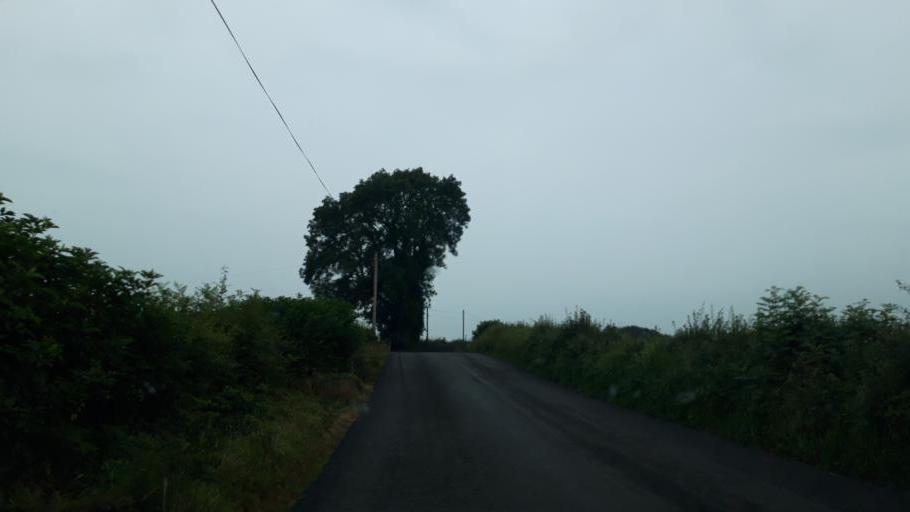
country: IE
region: Leinster
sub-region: Kilkenny
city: Thomastown
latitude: 52.6079
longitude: -7.1210
